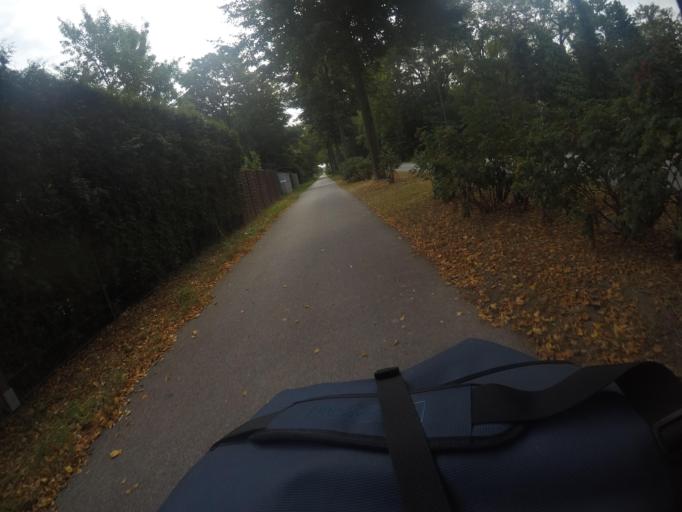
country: DE
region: North Rhine-Westphalia
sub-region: Regierungsbezirk Dusseldorf
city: Emmerich
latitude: 51.8471
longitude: 6.2066
